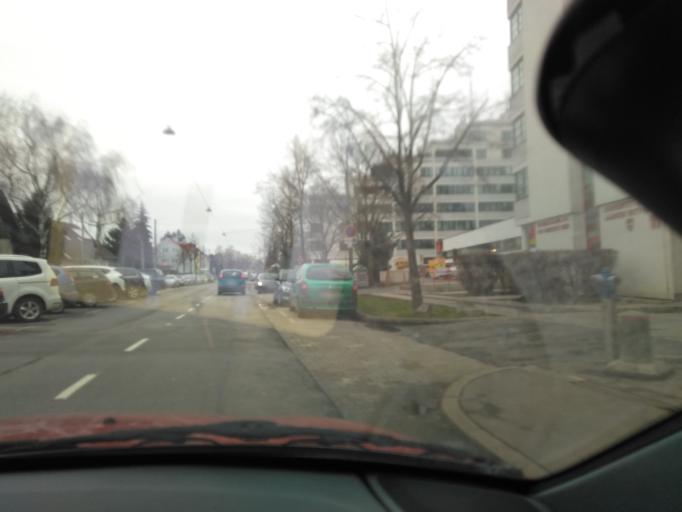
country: AT
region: Lower Austria
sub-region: Politischer Bezirk Modling
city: Vosendorf
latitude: 48.1608
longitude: 16.3282
